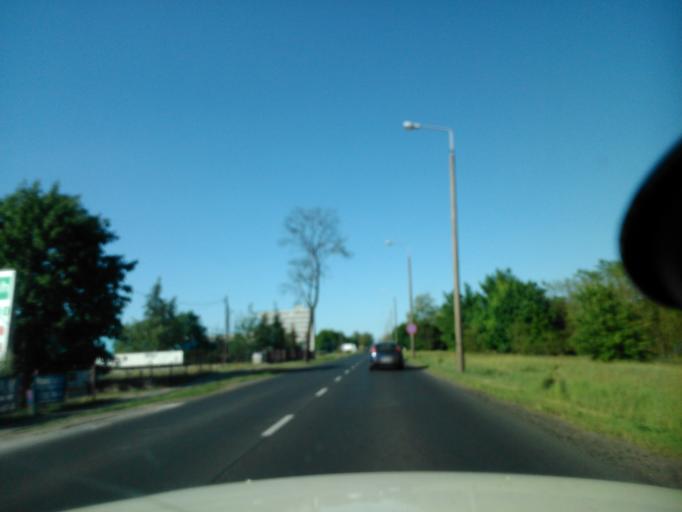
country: PL
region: Kujawsko-Pomorskie
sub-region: Torun
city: Torun
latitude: 52.9832
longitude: 18.5758
